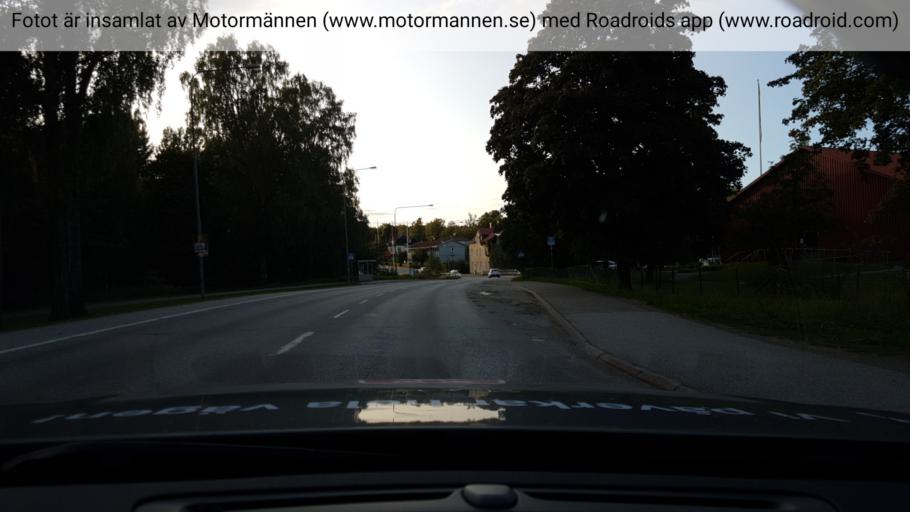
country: SE
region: OErebro
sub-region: Ljusnarsbergs Kommun
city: Kopparberg
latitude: 59.8732
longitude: 15.0032
